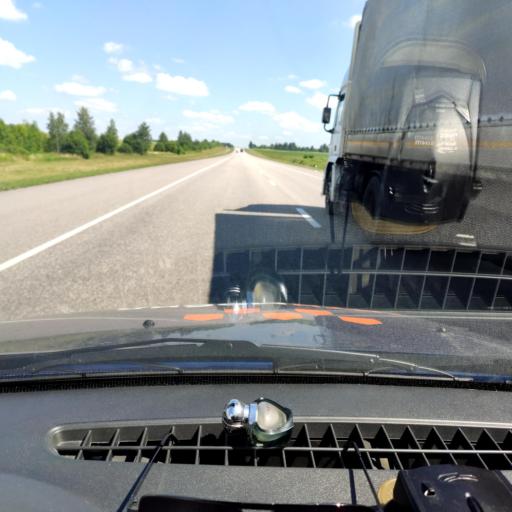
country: RU
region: Orjol
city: Orel
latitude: 52.8553
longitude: 36.2222
